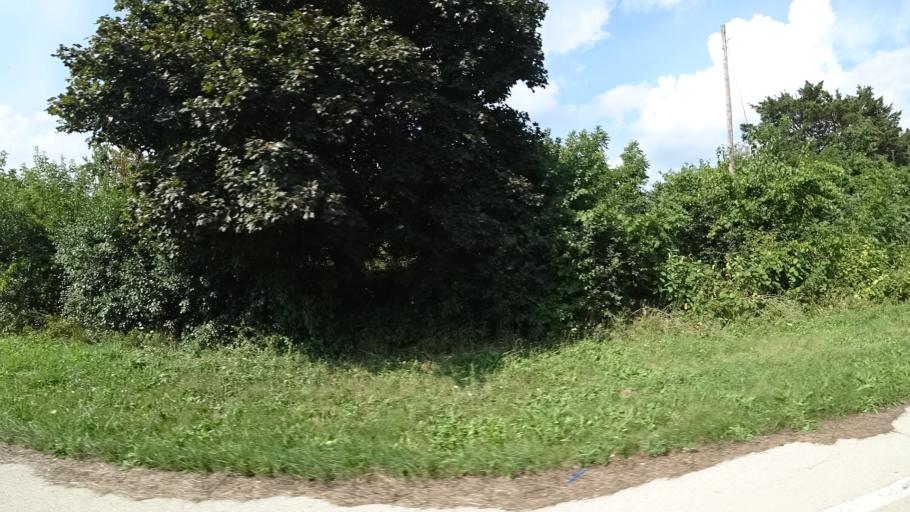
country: US
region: Illinois
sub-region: Will County
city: Goodings Grove
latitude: 41.6510
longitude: -87.9273
